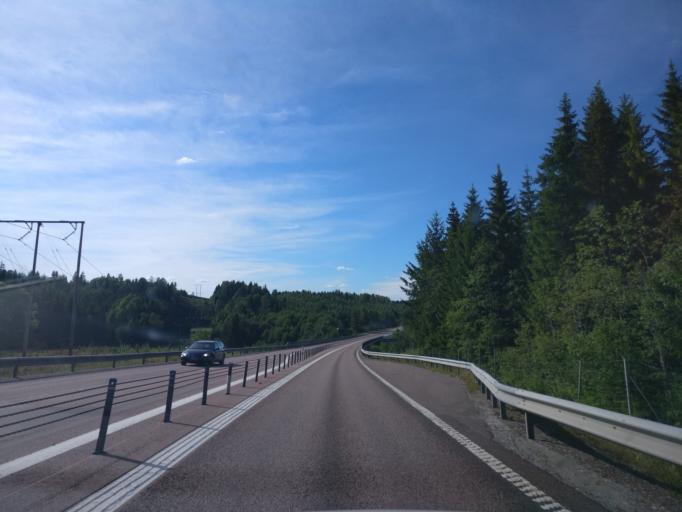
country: SE
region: Vaermland
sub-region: Kils Kommun
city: Kil
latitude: 59.5028
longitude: 13.2590
